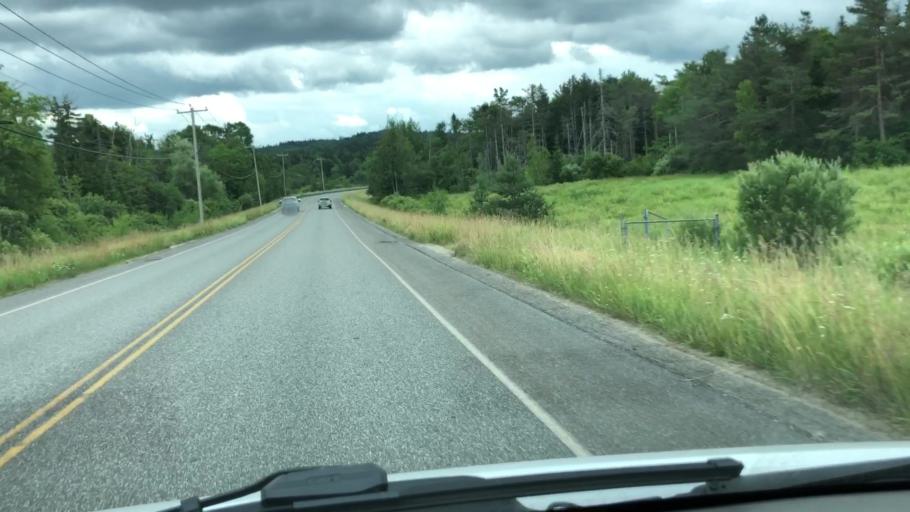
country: US
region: Massachusetts
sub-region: Berkshire County
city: Adams
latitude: 42.5330
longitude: -73.0571
